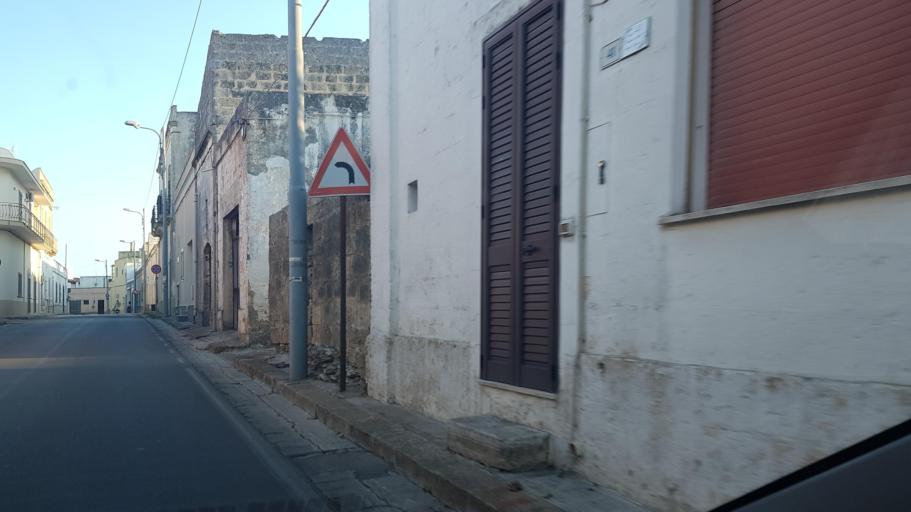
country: IT
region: Apulia
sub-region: Provincia di Lecce
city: Lucugnano
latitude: 39.9361
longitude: 18.3193
